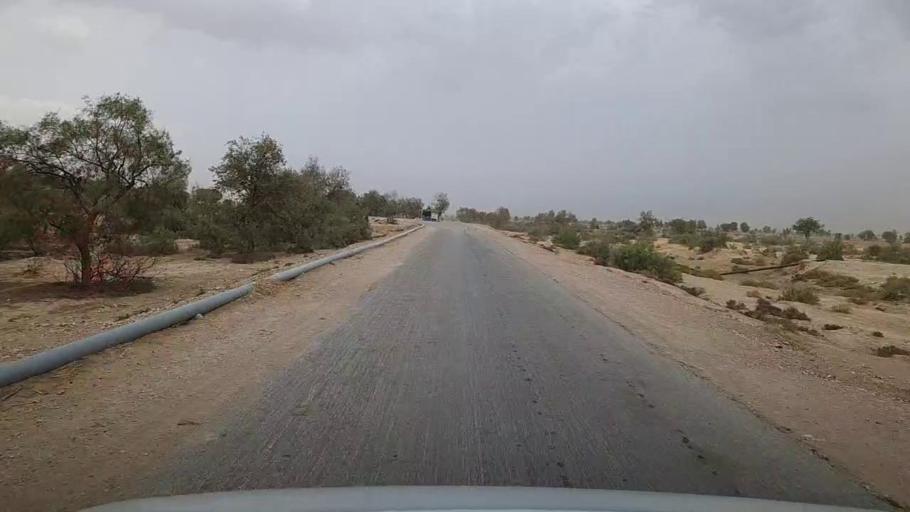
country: PK
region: Sindh
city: Sehwan
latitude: 26.3243
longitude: 67.7263
